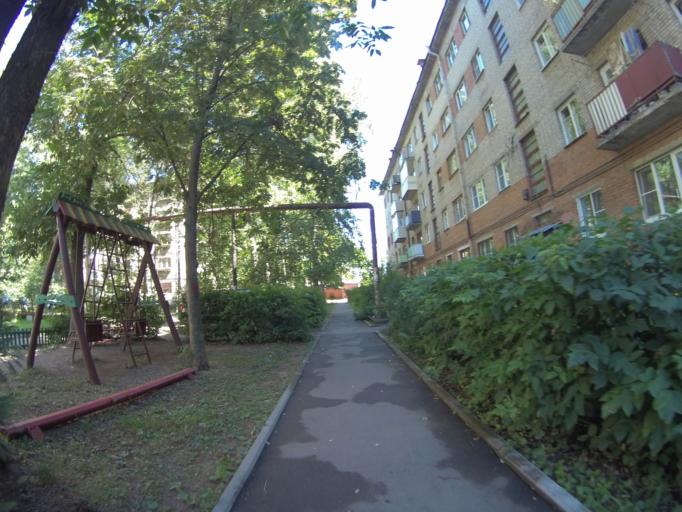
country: RU
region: Vladimir
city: Vladimir
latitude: 56.1285
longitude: 40.3613
